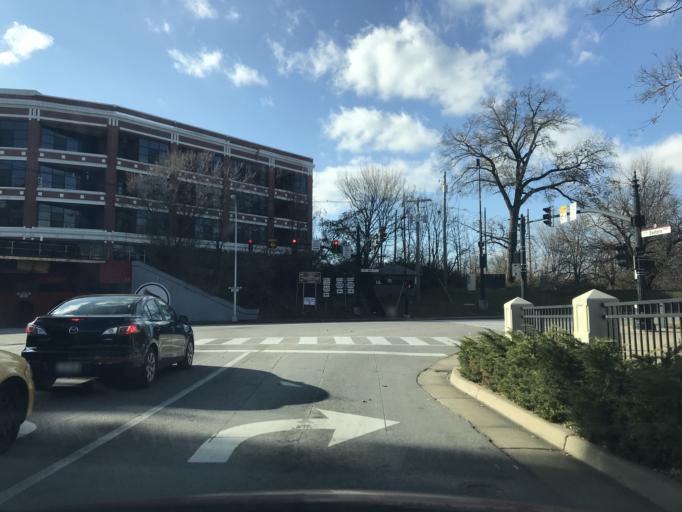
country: US
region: Kentucky
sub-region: Jefferson County
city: Audubon Park
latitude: 38.2138
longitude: -85.7619
